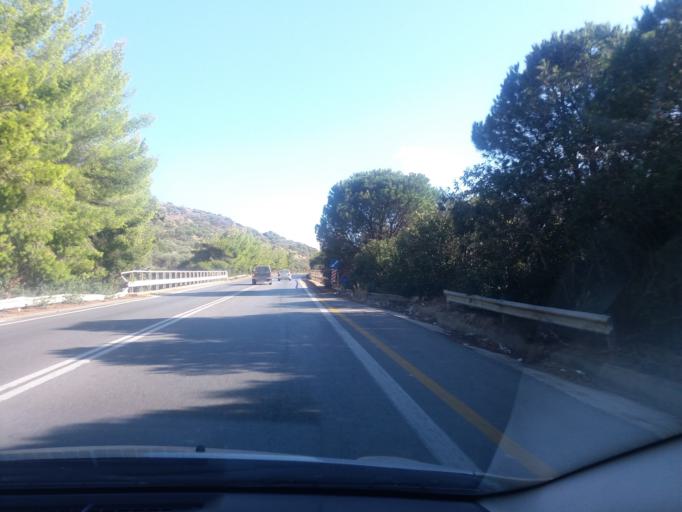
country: GR
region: Crete
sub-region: Nomos Lasithiou
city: Sision
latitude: 35.2833
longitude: 25.5455
